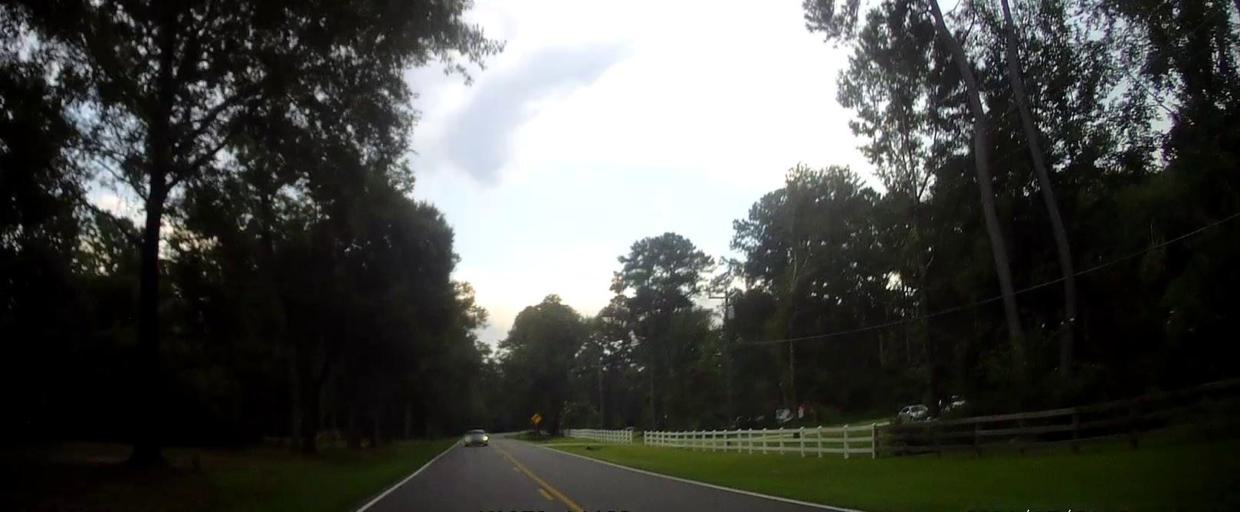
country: US
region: Georgia
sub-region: Laurens County
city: Dublin
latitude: 32.5815
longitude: -82.9035
